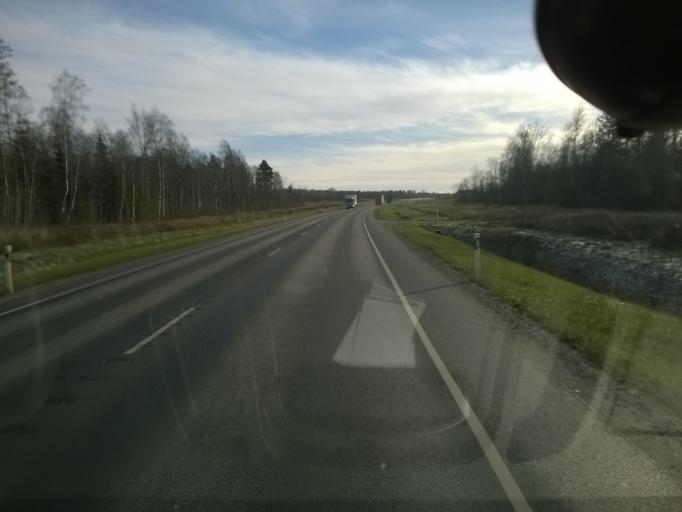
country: EE
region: Harju
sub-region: Saue vald
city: Laagri
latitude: 59.3273
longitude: 24.6348
